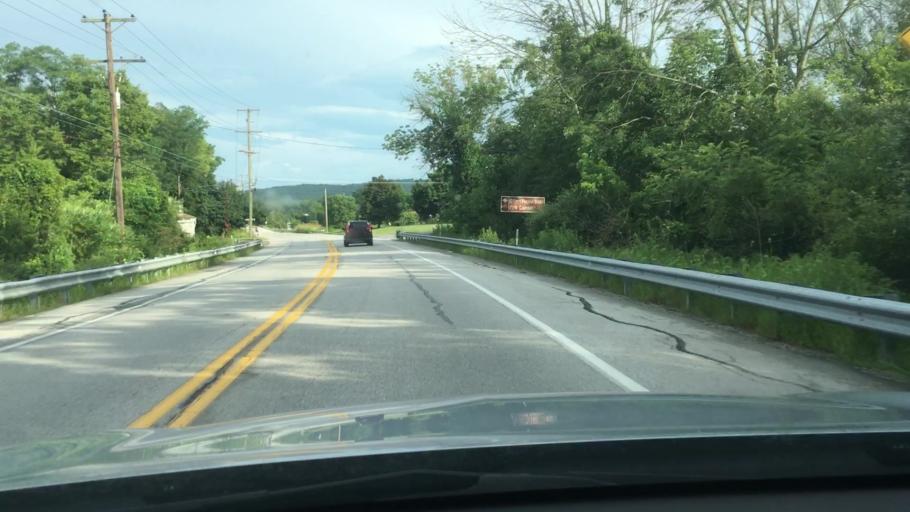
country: US
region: Pennsylvania
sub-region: York County
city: Dover
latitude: 40.0551
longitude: -76.9112
